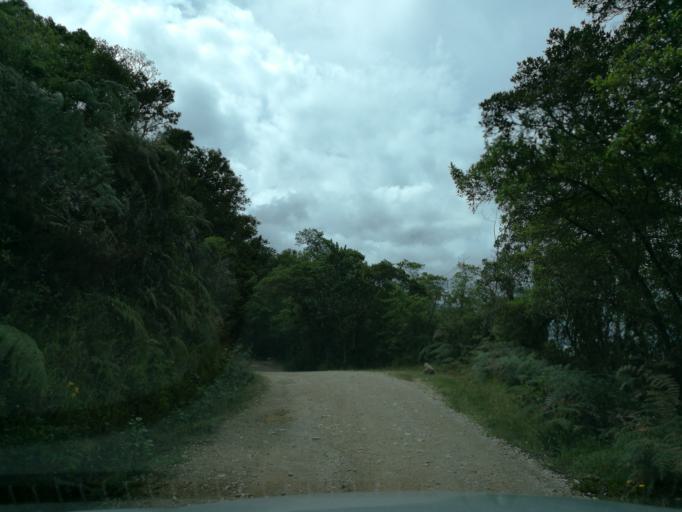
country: CO
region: Boyaca
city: Arcabuco
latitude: 5.7534
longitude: -73.4532
